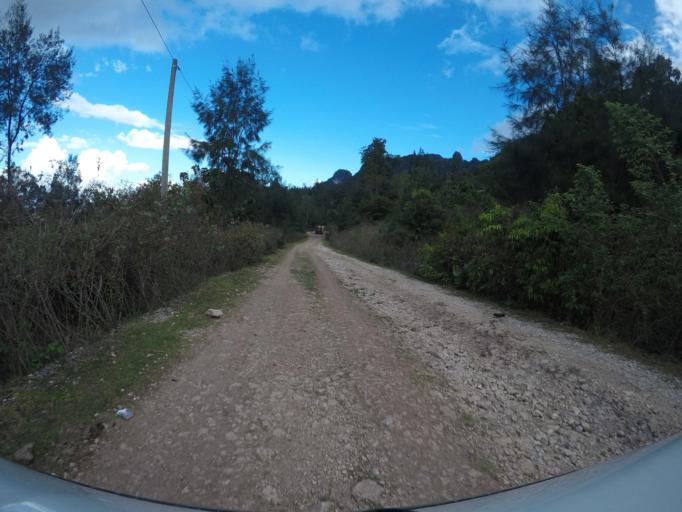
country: TL
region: Baucau
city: Venilale
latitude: -8.6855
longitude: 126.6565
